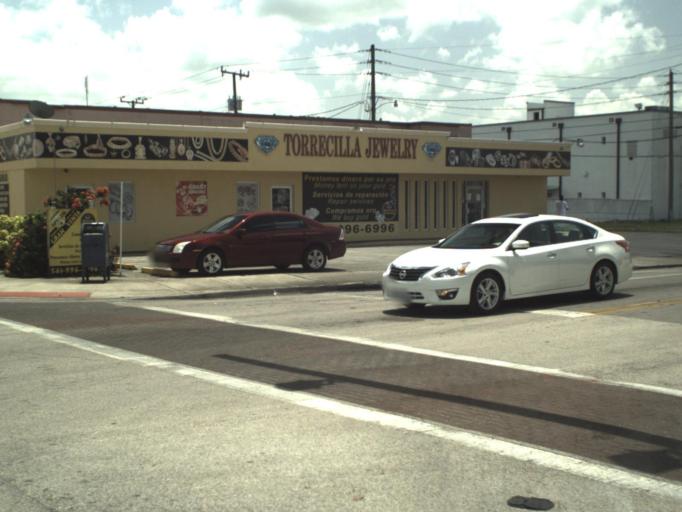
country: US
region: Florida
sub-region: Palm Beach County
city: Belle Glade
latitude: 26.6858
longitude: -80.6679
